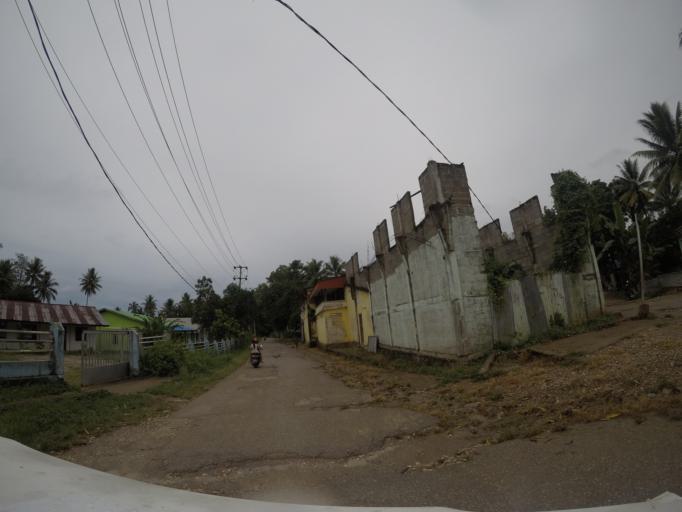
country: TL
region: Lautem
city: Lospalos
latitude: -8.5247
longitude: 126.9974
